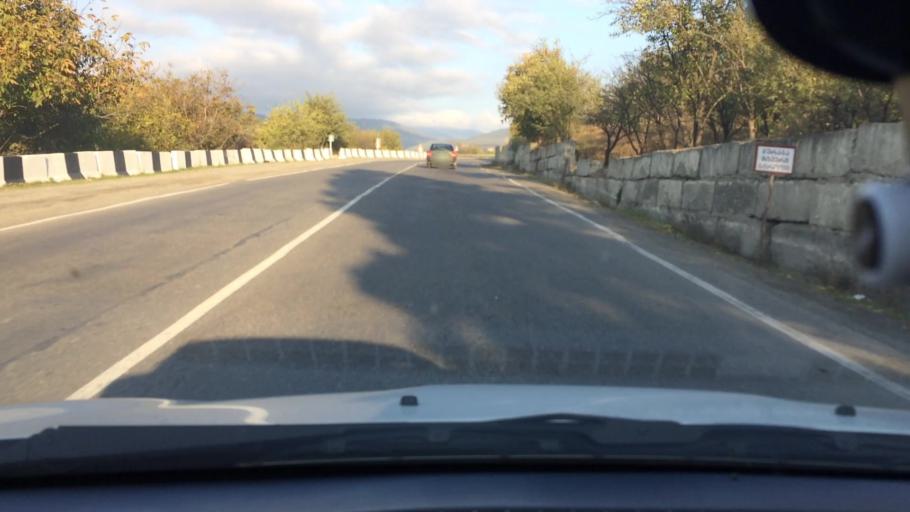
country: GE
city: Surami
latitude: 42.0173
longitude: 43.5685
